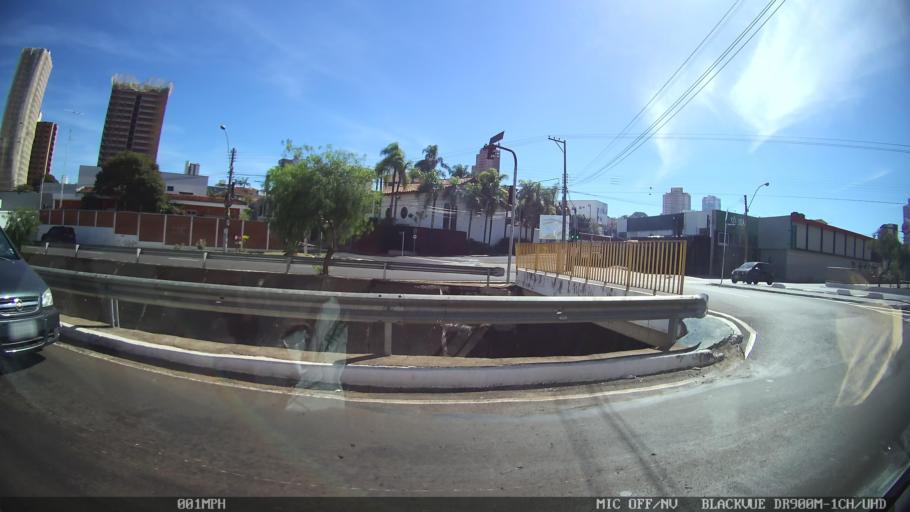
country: BR
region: Sao Paulo
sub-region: Franca
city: Franca
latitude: -20.5392
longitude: -47.3928
